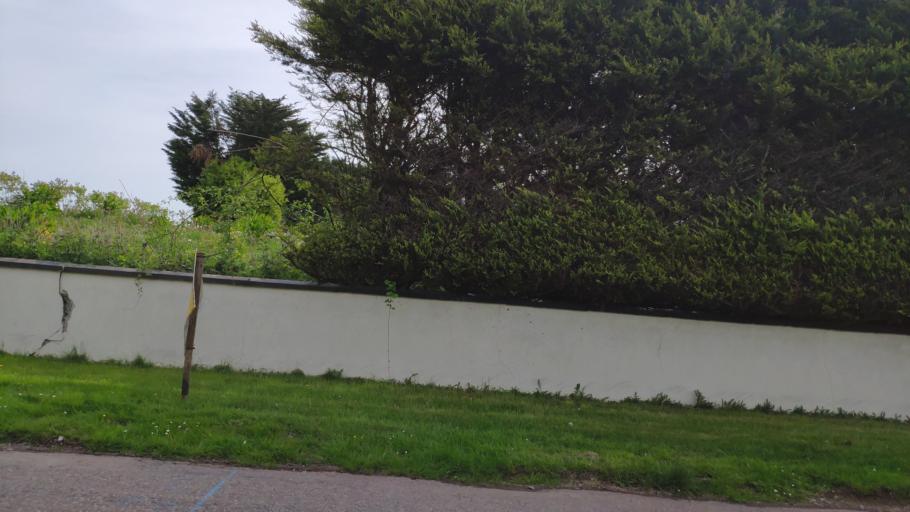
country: IE
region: Munster
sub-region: County Cork
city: Blarney
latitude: 51.9761
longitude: -8.5135
